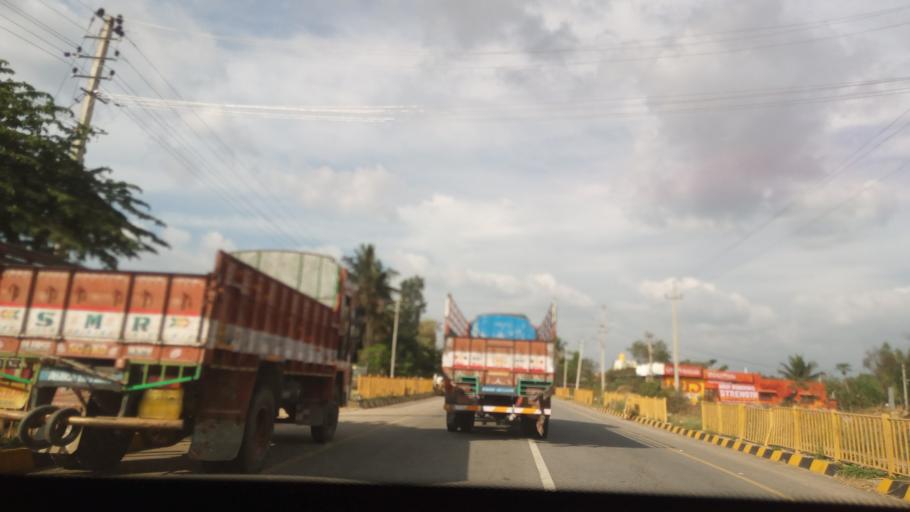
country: IN
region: Karnataka
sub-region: Mandya
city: Maddur
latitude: 12.6675
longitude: 77.0545
